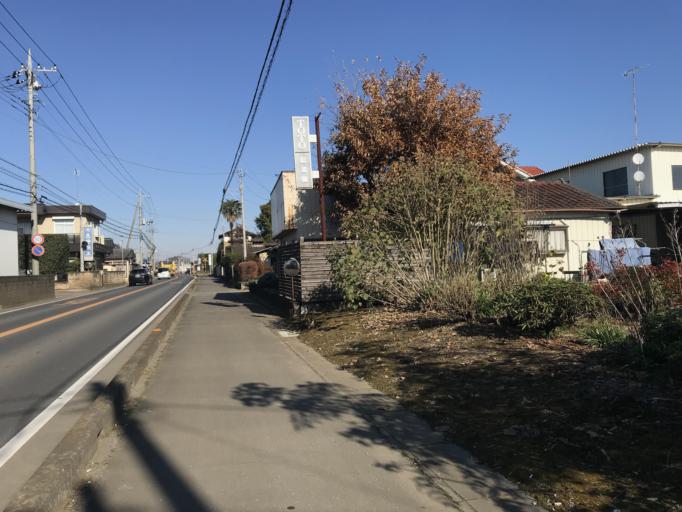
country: JP
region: Tochigi
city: Oyama
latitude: 36.2564
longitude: 139.8377
